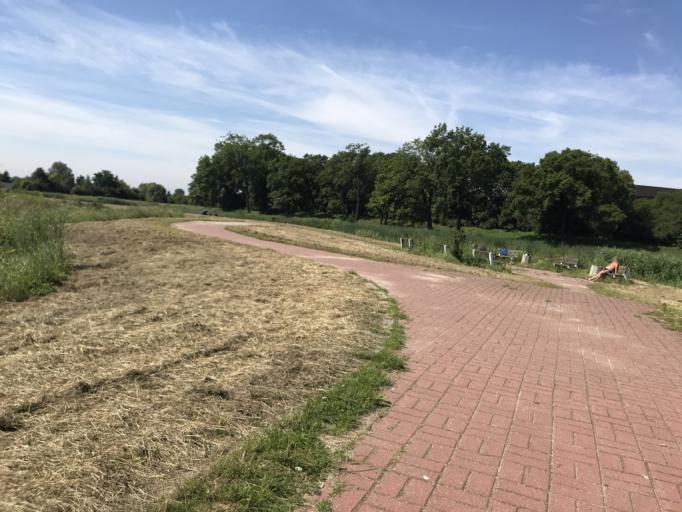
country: PL
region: Pomeranian Voivodeship
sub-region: Gdansk
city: Gdansk
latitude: 54.3407
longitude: 18.6657
